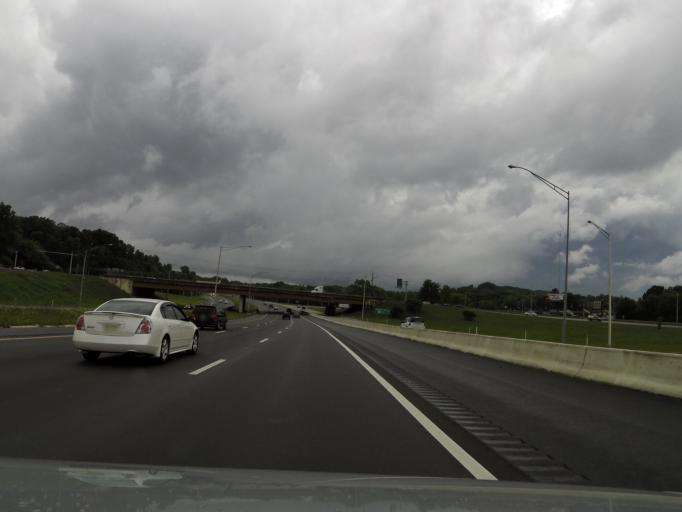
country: US
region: Tennessee
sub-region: Knox County
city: Knoxville
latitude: 35.9721
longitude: -83.9794
